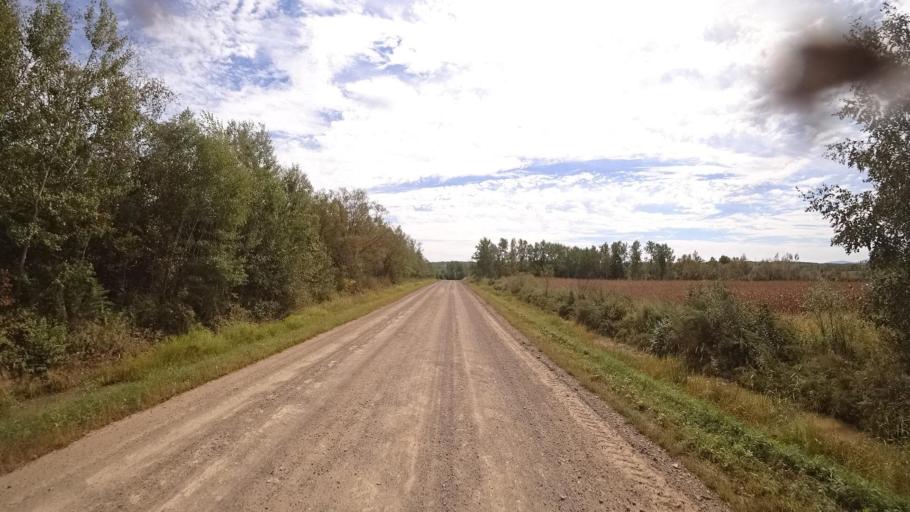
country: RU
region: Primorskiy
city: Yakovlevka
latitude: 44.5646
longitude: 133.5958
